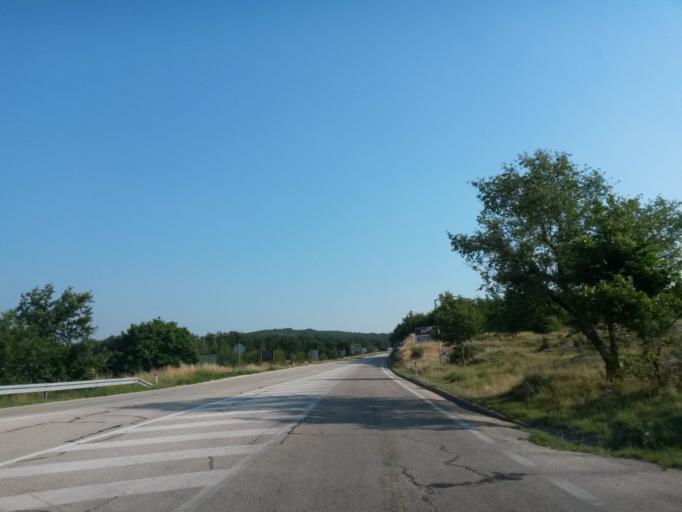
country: BA
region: Federation of Bosnia and Herzegovina
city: Podhum
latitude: 43.6179
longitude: 17.0000
